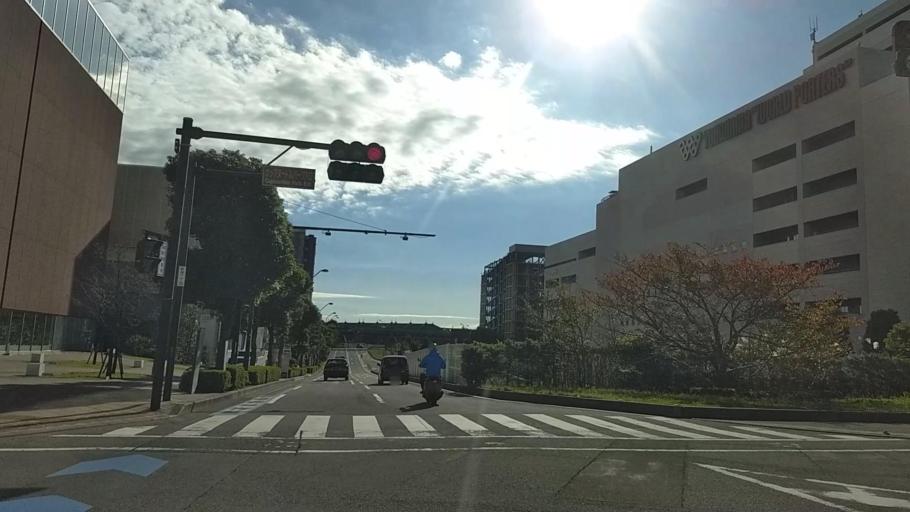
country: JP
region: Kanagawa
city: Yokohama
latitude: 35.4552
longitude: 139.6384
